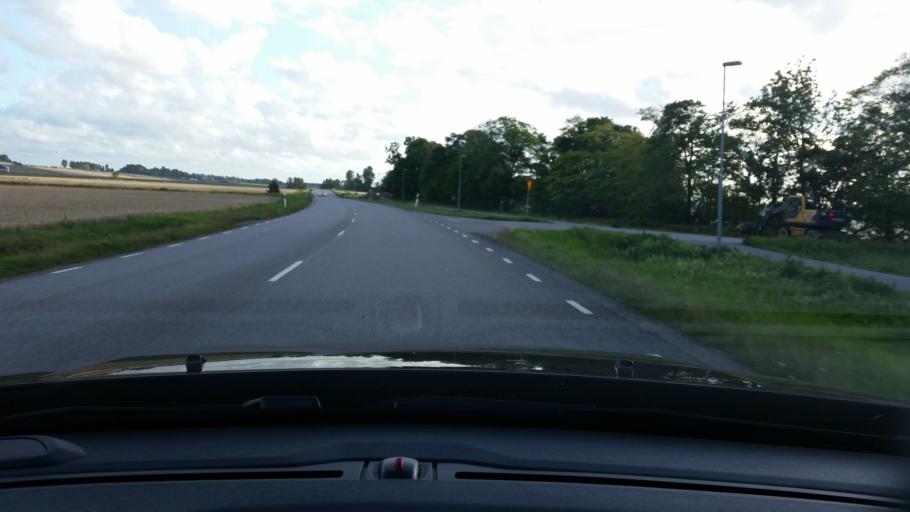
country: SE
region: Vaestra Goetaland
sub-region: Vanersborgs Kommun
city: Vargon
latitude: 58.3458
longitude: 12.3846
